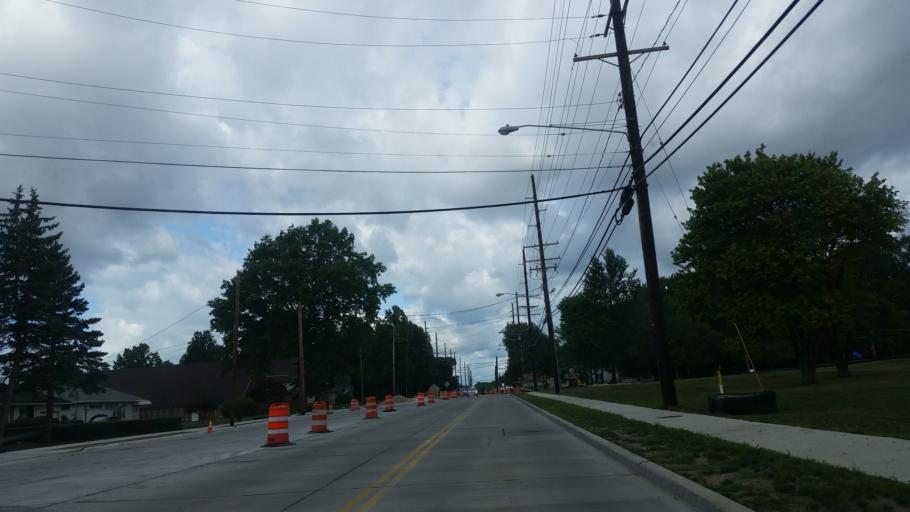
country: US
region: Ohio
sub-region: Cuyahoga County
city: Parma Heights
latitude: 41.3640
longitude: -81.7732
